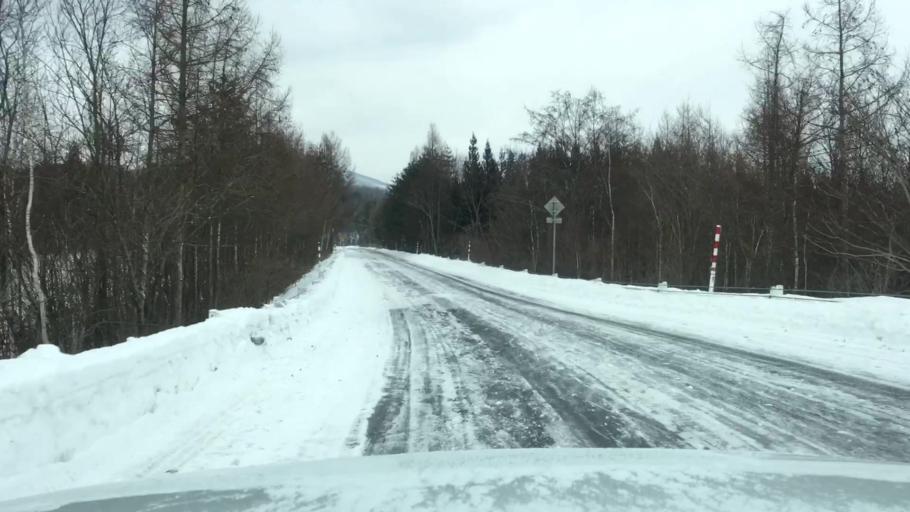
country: JP
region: Iwate
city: Shizukuishi
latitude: 39.9368
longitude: 141.0019
